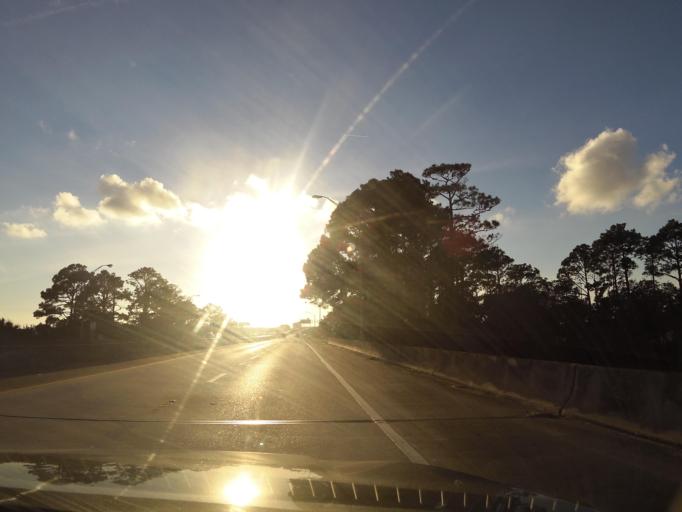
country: US
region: Florida
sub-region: Saint Johns County
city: Ponte Vedra Beach
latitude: 30.2589
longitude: -81.4131
